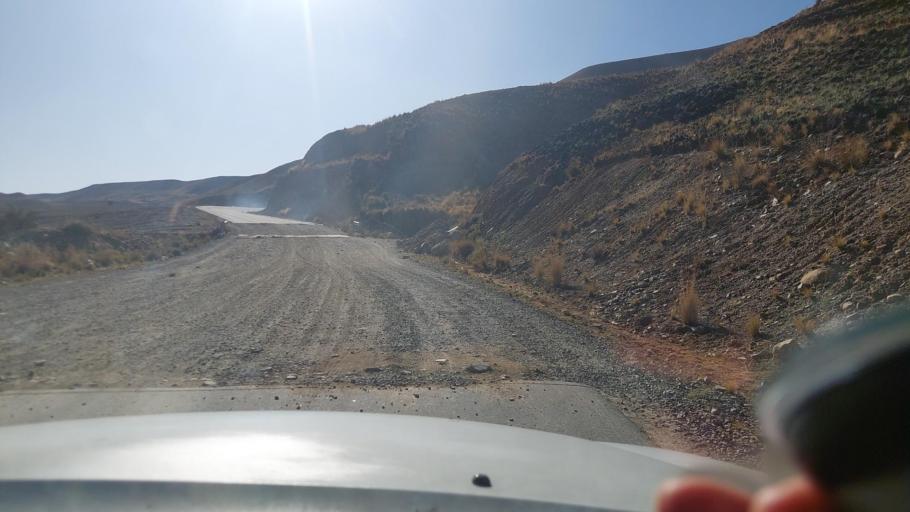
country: BO
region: La Paz
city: La Paz
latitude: -16.4219
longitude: -68.1209
